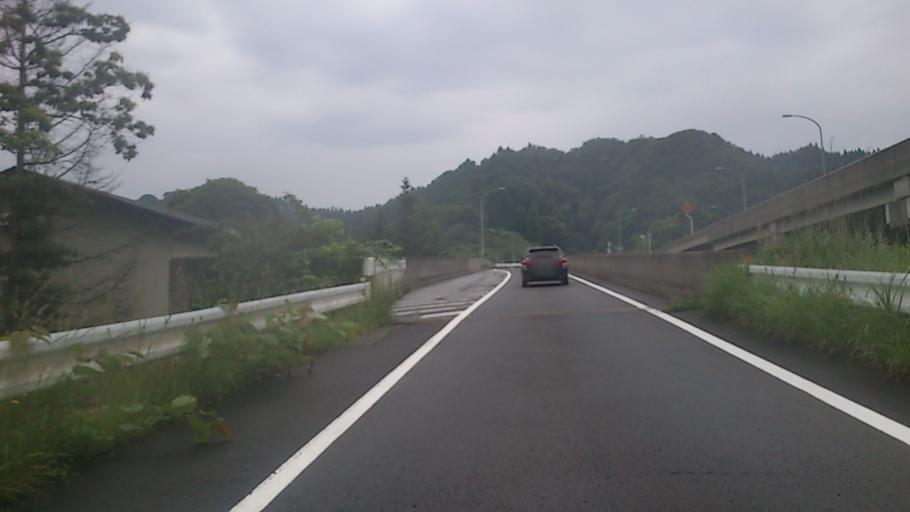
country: JP
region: Akita
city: Takanosu
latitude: 40.2183
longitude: 140.2447
